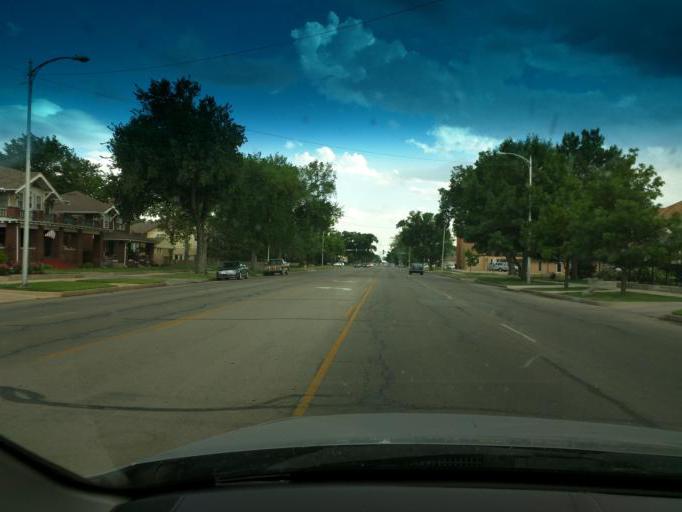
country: US
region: Kansas
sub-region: Reno County
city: Hutchinson
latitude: 38.0738
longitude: -97.9320
